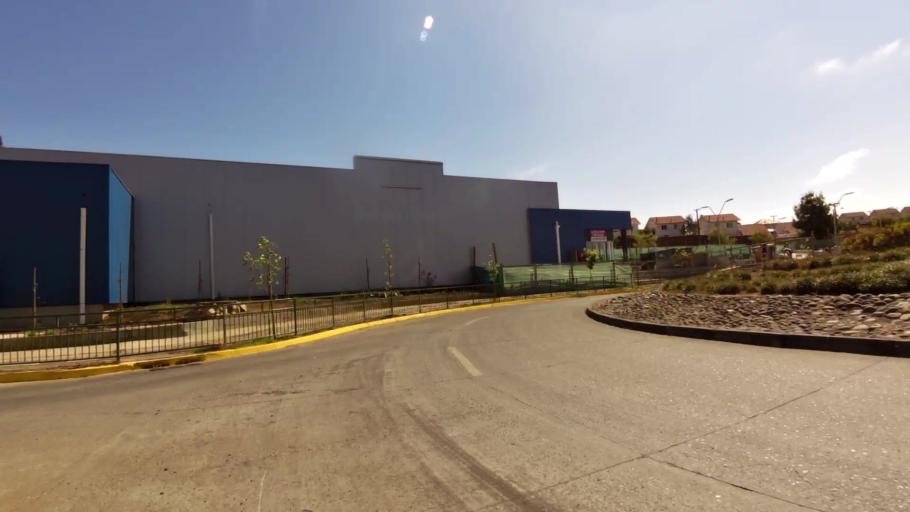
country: CL
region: Biobio
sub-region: Provincia de Concepcion
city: Concepcion
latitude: -36.7863
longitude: -73.0372
